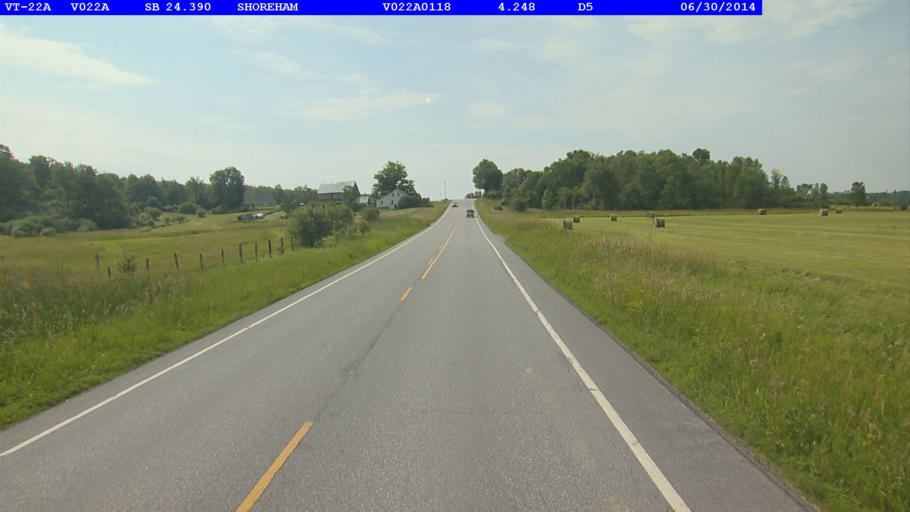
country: US
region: New York
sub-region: Essex County
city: Ticonderoga
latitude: 43.9105
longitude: -73.3103
